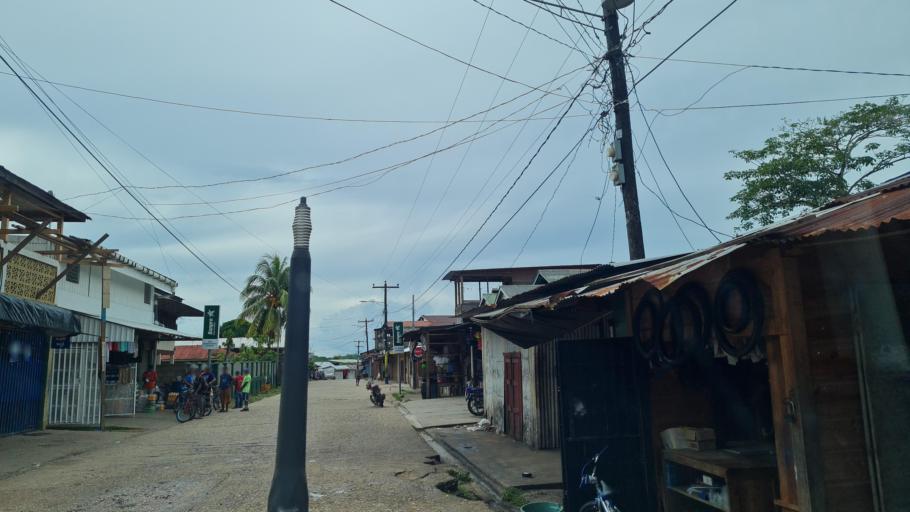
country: NI
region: Atlantico Norte (RAAN)
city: Waspam
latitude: 14.7435
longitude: -83.9717
